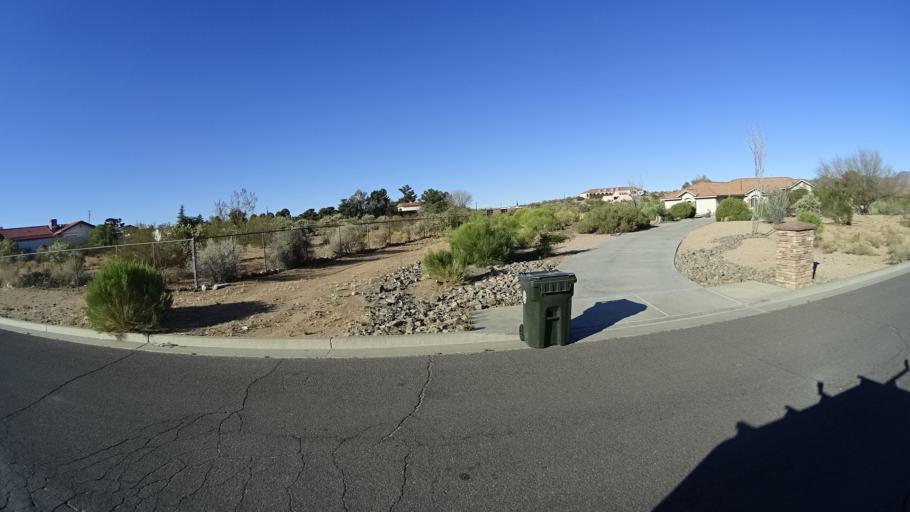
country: US
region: Arizona
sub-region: Mohave County
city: Kingman
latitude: 35.2042
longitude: -113.9975
